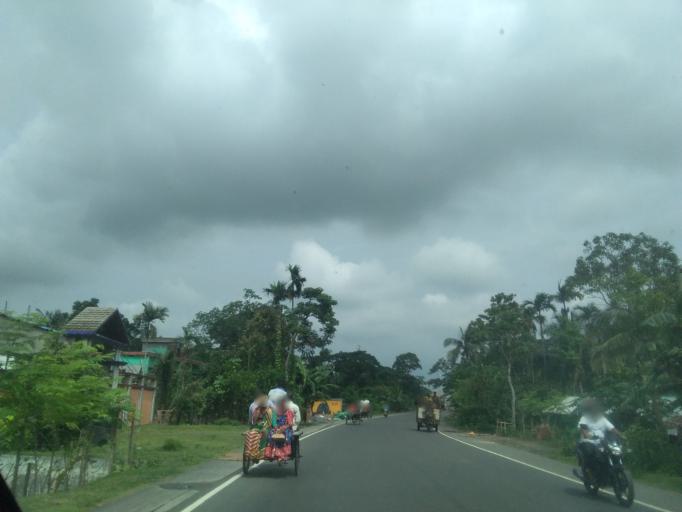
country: BD
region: Khulna
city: Kesabpur
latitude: 22.8374
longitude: 89.3022
